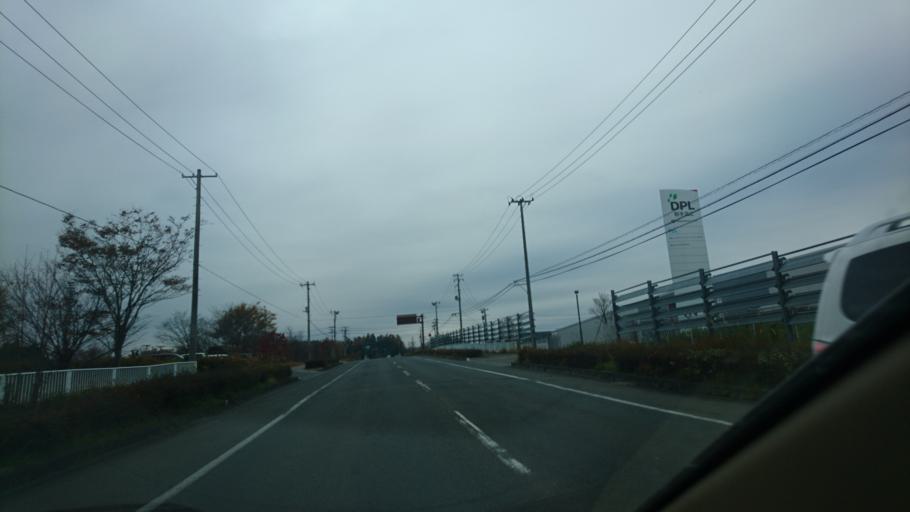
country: JP
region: Iwate
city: Kitakami
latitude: 39.2386
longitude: 141.0865
